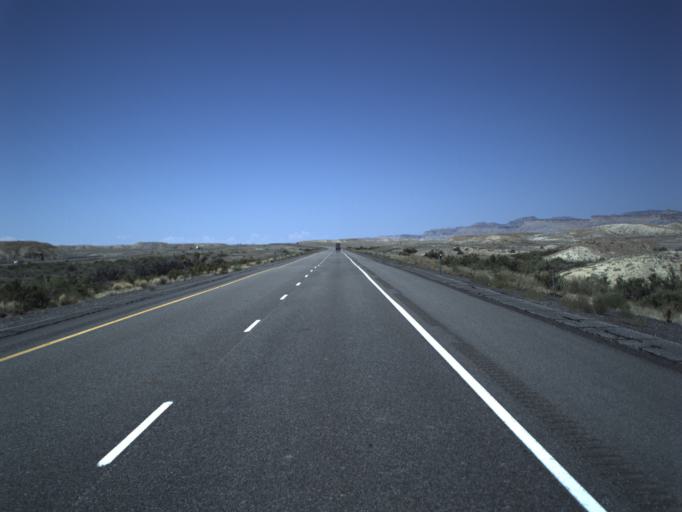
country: US
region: Utah
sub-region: Grand County
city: Moab
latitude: 38.9412
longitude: -109.5141
